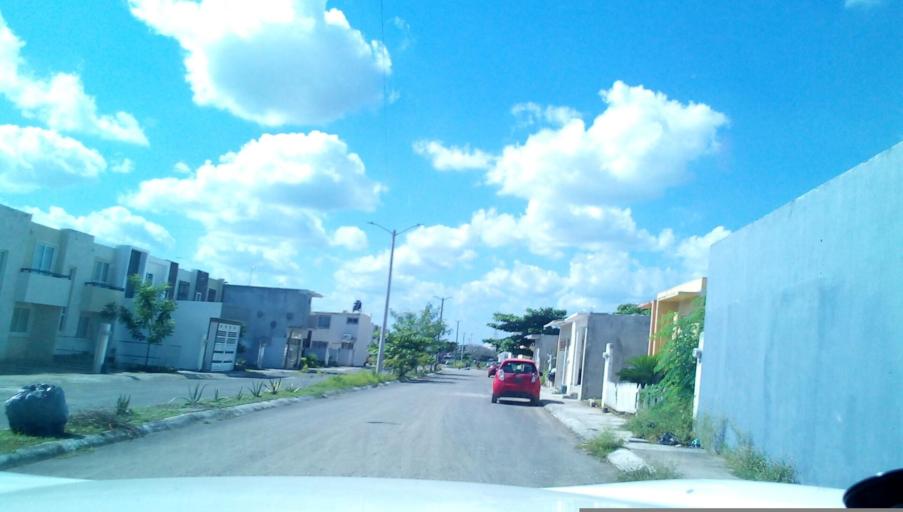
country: MX
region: Veracruz
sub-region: Veracruz
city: Las Amapolas
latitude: 19.1530
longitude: -96.2162
